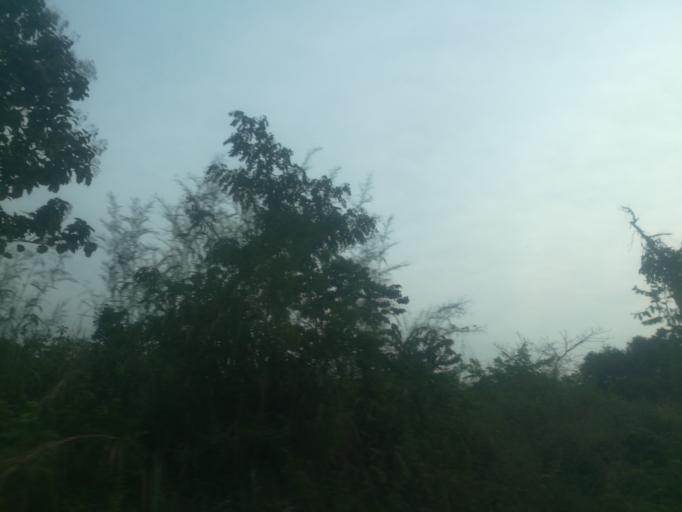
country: NG
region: Ogun
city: Abeokuta
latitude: 7.1980
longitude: 3.2247
